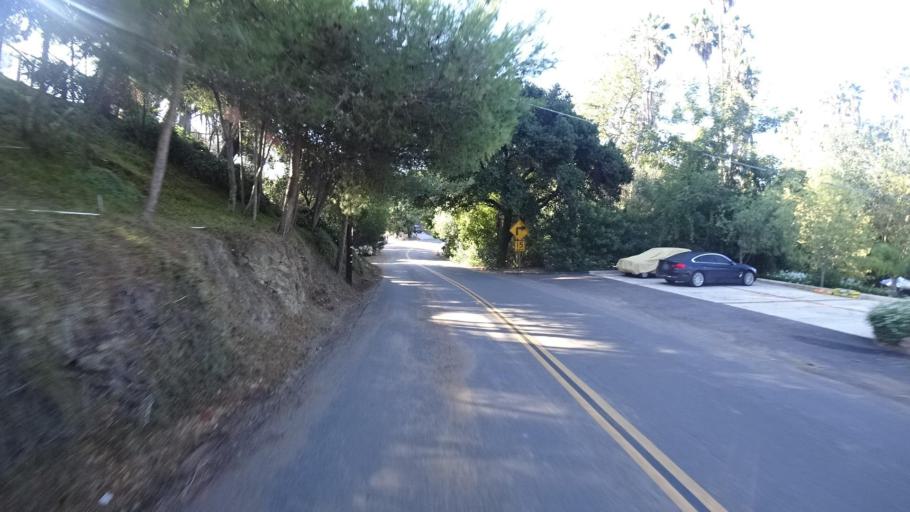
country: US
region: California
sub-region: San Diego County
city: Casa de Oro-Mount Helix
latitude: 32.7711
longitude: -116.9936
